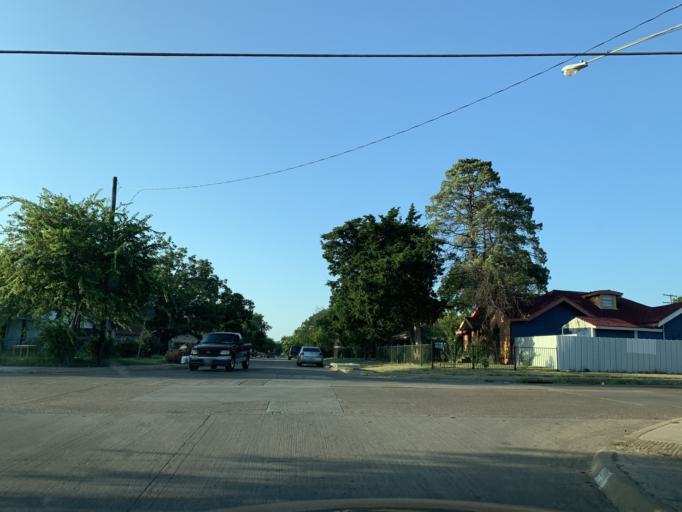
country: US
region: Texas
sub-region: Dallas County
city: Dallas
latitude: 32.7130
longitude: -96.8072
